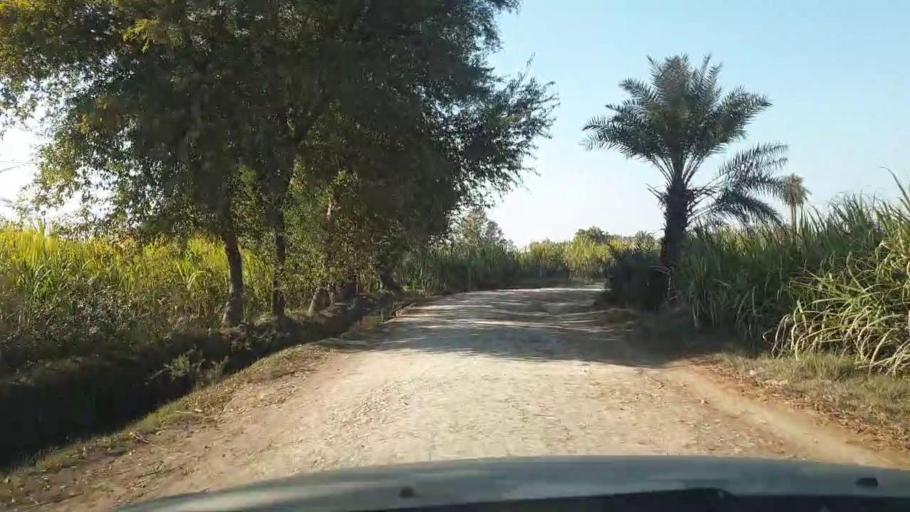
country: PK
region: Sindh
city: Ghotki
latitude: 28.0577
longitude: 69.3381
